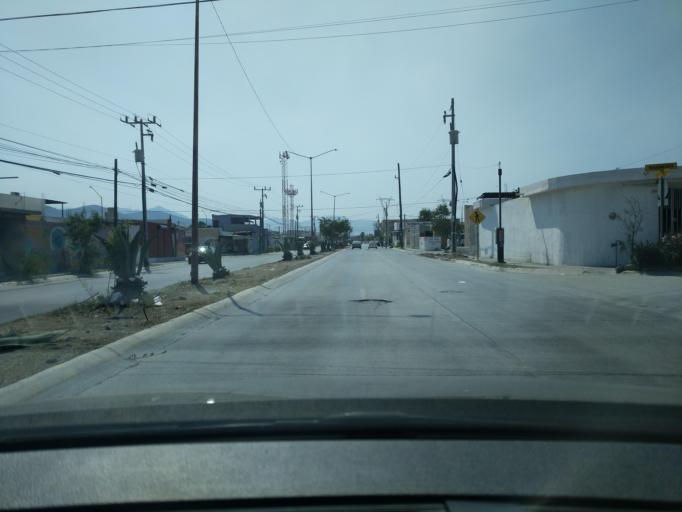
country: MX
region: Nuevo Leon
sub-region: Garcia
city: Valle de Lincoln
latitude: 25.7914
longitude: -100.4851
